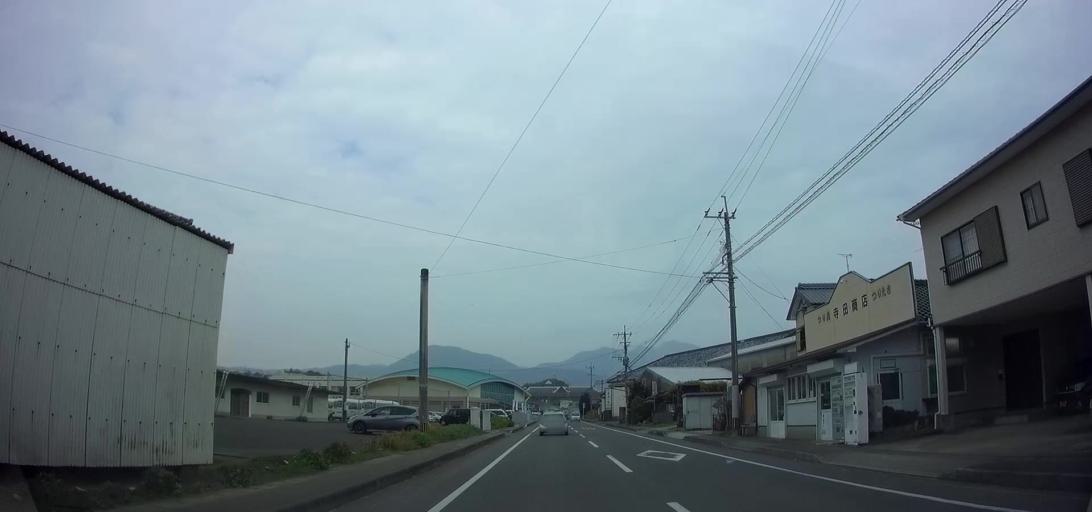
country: JP
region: Nagasaki
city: Shimabara
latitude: 32.6560
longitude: 130.2987
